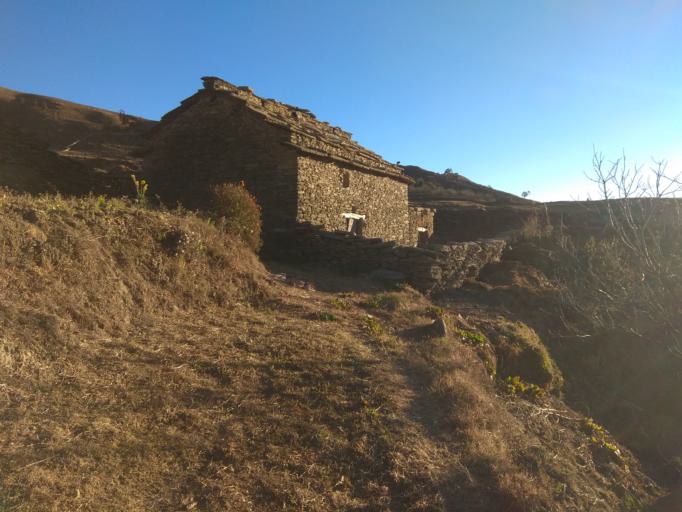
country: NP
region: Far Western
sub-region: Seti Zone
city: Achham
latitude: 29.2742
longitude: 81.6457
